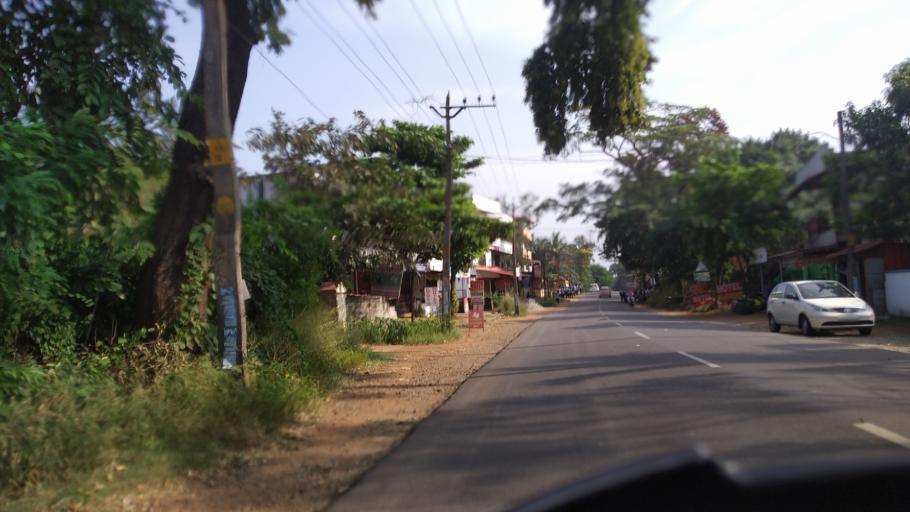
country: IN
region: Kerala
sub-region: Thrissur District
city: Chelakara
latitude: 10.5962
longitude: 76.5018
